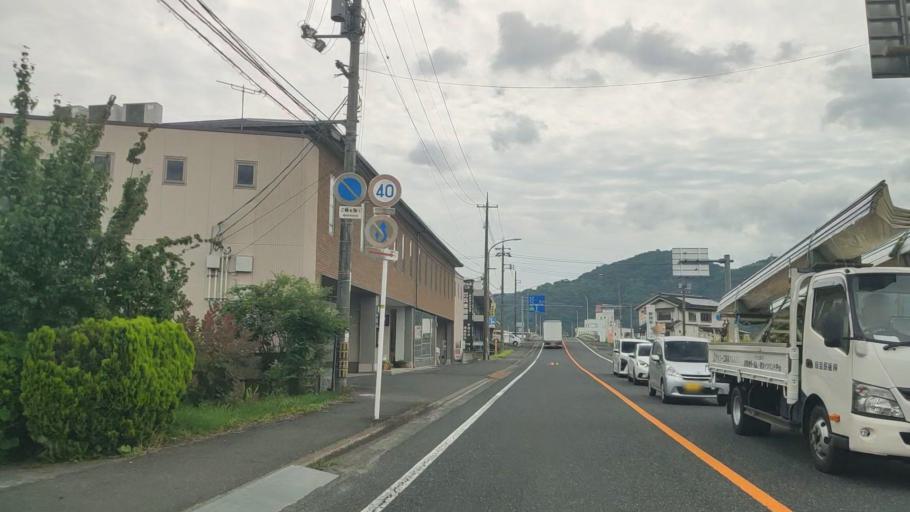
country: JP
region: Okayama
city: Tsuyama
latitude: 35.0607
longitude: 133.9788
